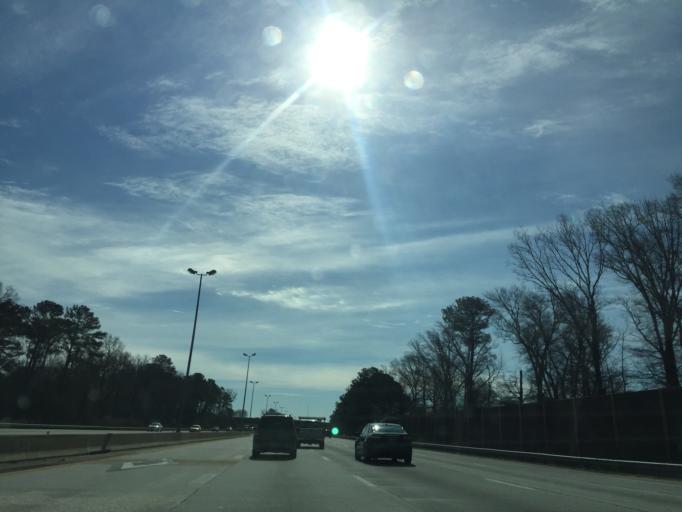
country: US
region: Virginia
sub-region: City of Hampton
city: Hampton
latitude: 37.0547
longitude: -76.4110
